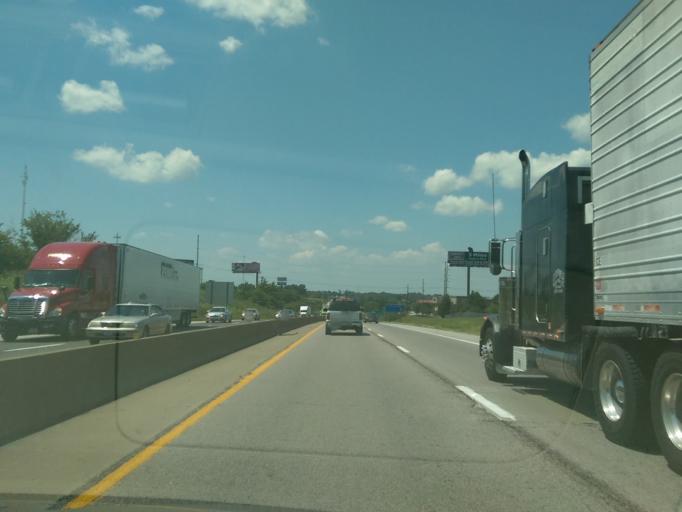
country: US
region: Missouri
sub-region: Boone County
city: Columbia
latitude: 38.9683
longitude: -92.3149
